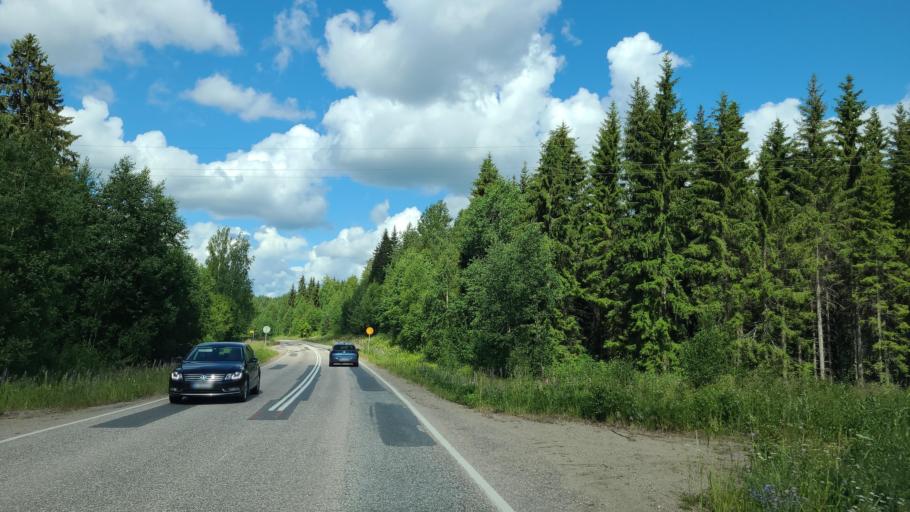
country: FI
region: Northern Savo
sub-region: Koillis-Savo
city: Kaavi
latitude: 62.9184
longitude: 28.7012
